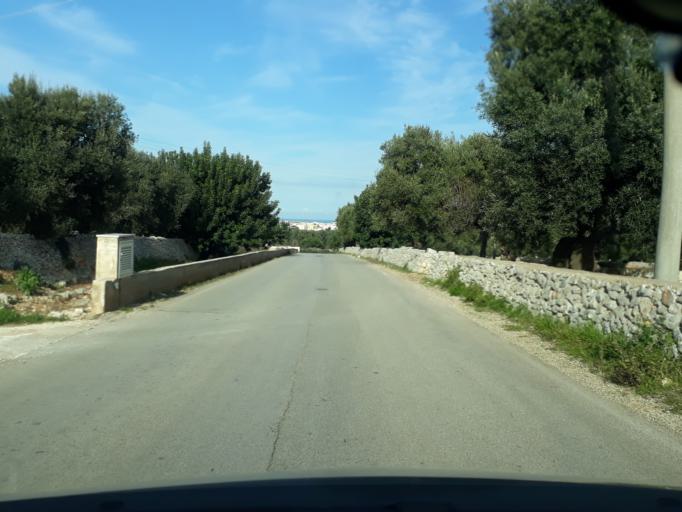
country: IT
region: Apulia
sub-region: Provincia di Brindisi
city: Fasano
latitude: 40.8192
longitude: 17.3578
